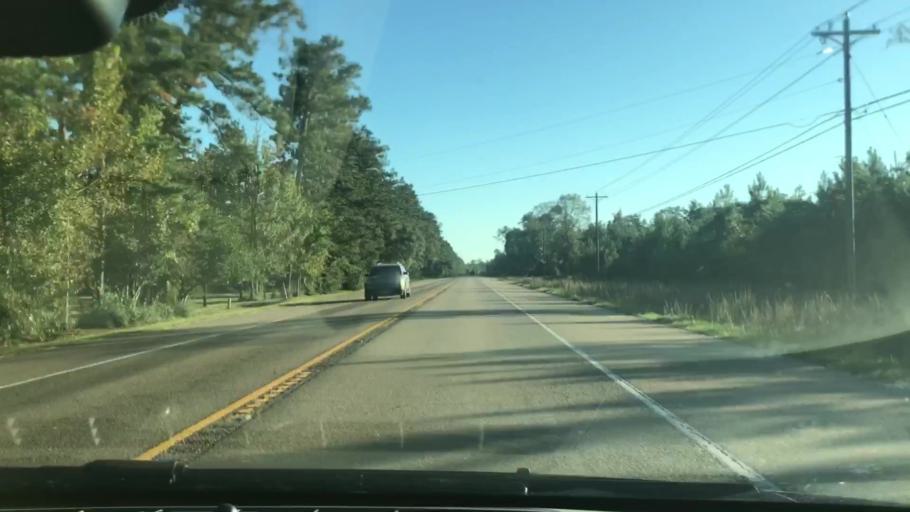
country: US
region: Louisiana
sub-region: Saint Tammany Parish
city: Abita Springs
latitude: 30.5709
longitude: -89.8714
